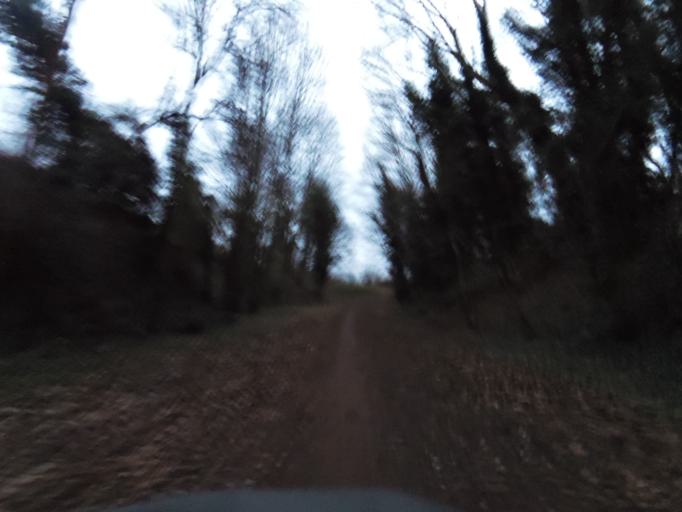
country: GB
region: England
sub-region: Norfolk
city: Costessey
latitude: 52.6765
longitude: 1.2193
